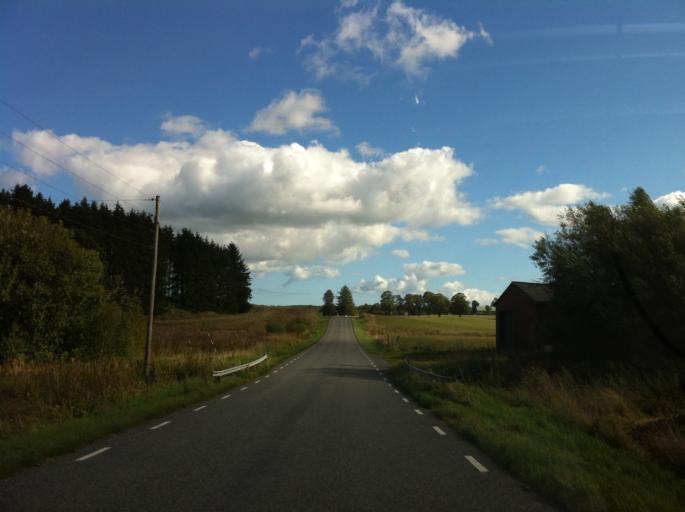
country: SE
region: Skane
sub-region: Kristianstads Kommun
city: Degeberga
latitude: 55.7044
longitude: 14.0082
